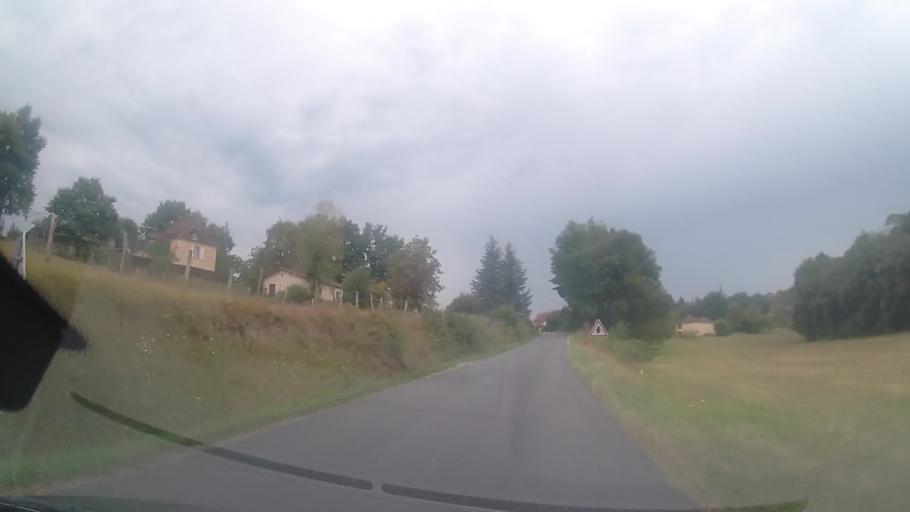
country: FR
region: Aquitaine
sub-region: Departement de la Dordogne
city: Carsac-Aillac
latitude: 44.8383
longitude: 1.2915
